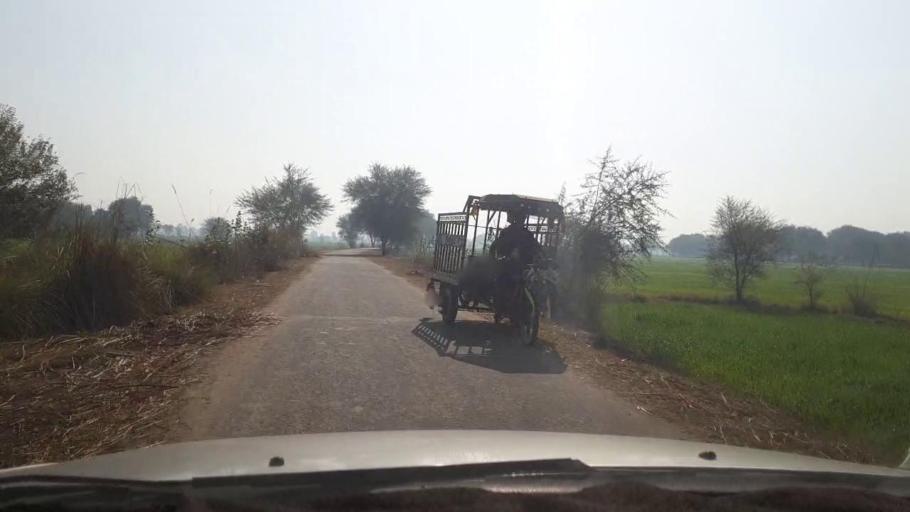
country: PK
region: Sindh
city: Khanpur
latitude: 27.7442
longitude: 69.5041
